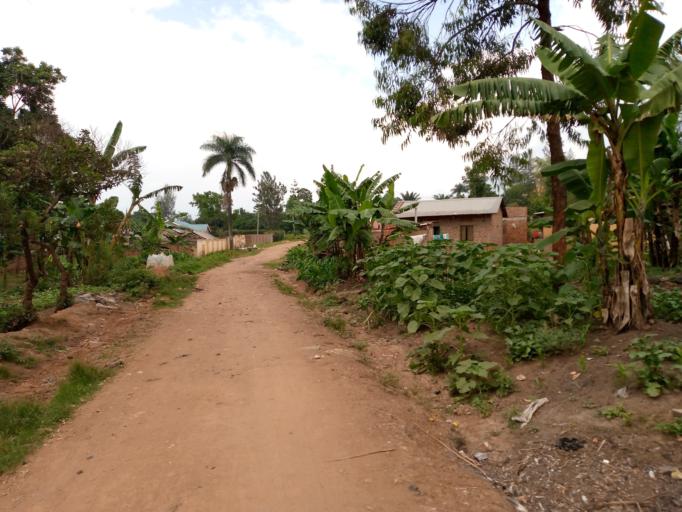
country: UG
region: Eastern Region
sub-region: Mbale District
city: Mbale
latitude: 1.0880
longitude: 34.1670
